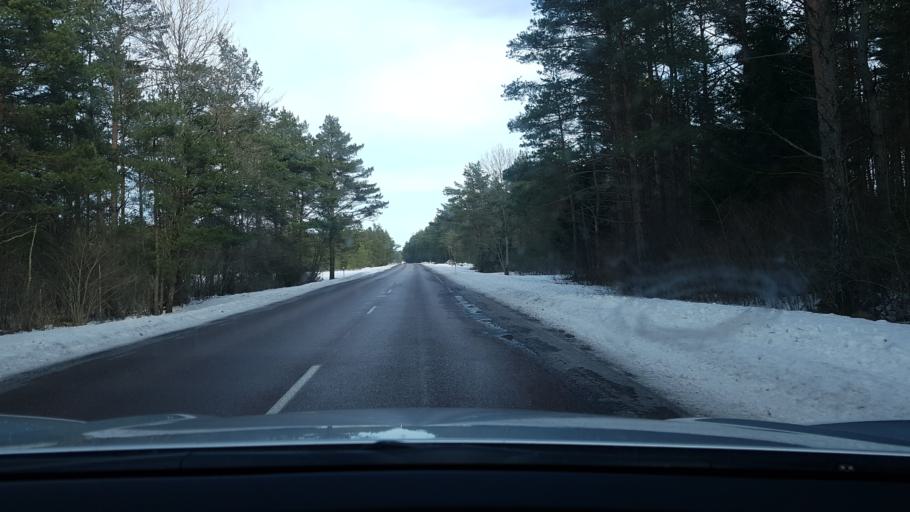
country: EE
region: Saare
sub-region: Kuressaare linn
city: Kuressaare
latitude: 58.3416
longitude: 22.5780
